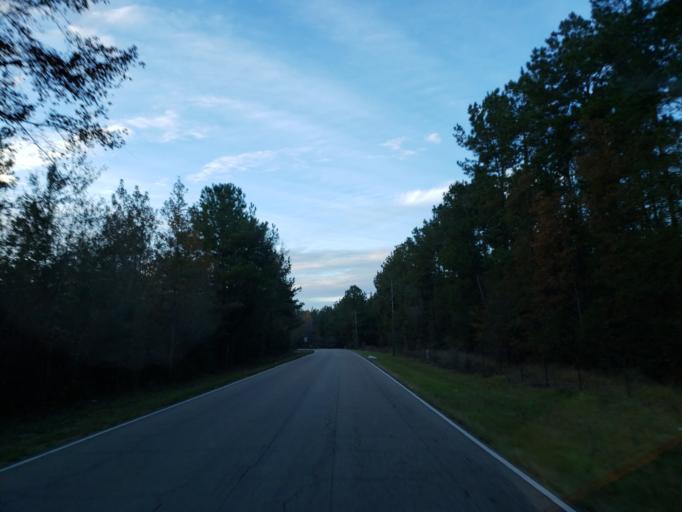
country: US
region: Mississippi
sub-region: Forrest County
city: Hattiesburg
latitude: 31.2775
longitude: -89.2470
